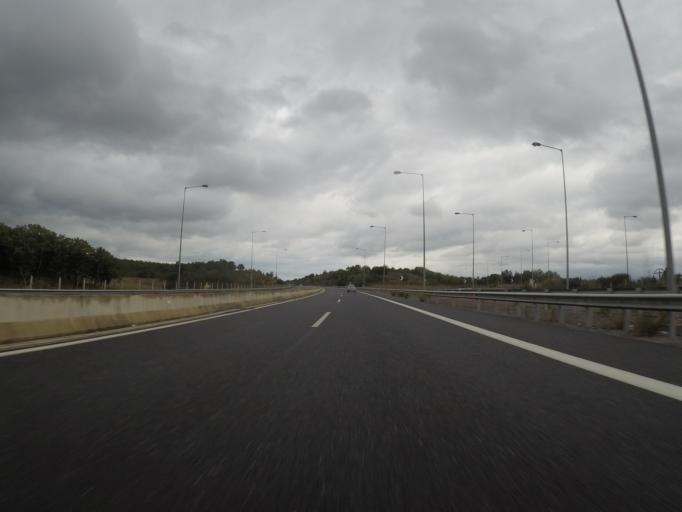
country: GR
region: Peloponnese
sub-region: Nomos Arkadias
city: Megalopoli
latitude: 37.3589
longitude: 22.1327
